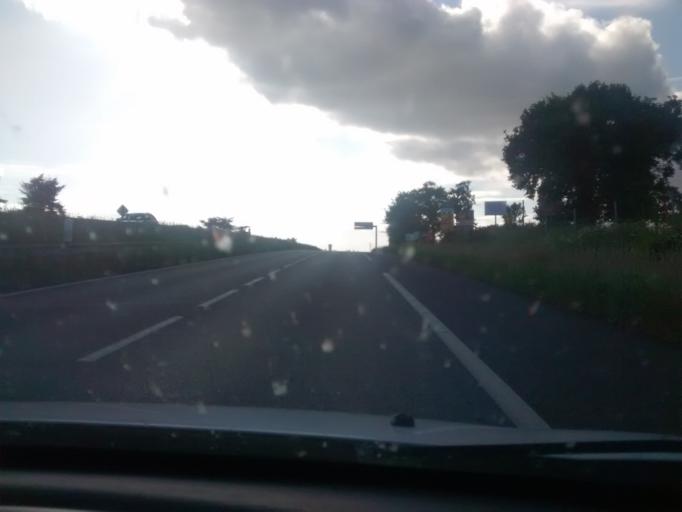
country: FR
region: Brittany
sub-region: Departement d'Ille-et-Vilaine
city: Brece
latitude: 48.1048
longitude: -1.4998
